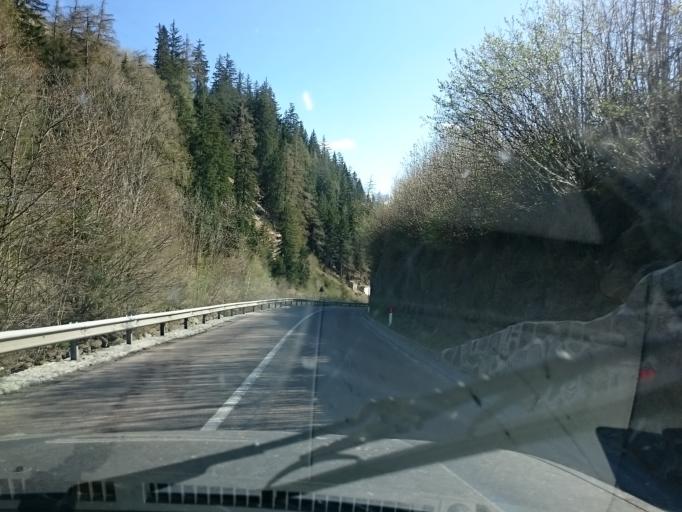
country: IT
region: Trentino-Alto Adige
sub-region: Bolzano
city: Colle Isarco
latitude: 46.9420
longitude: 11.4478
